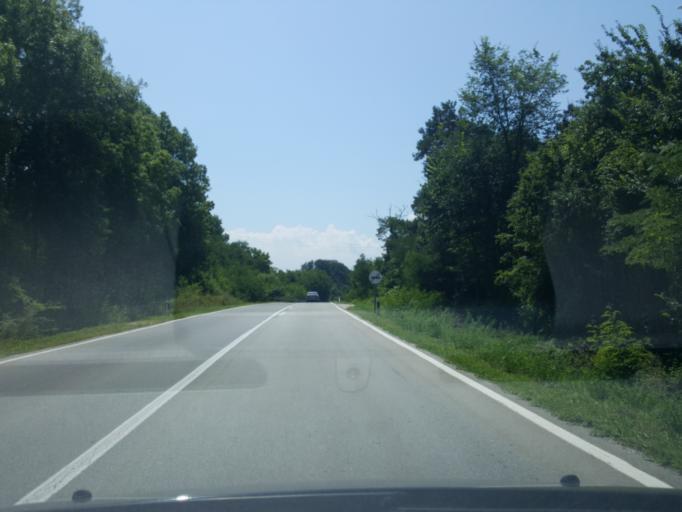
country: RS
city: Prislonica
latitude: 43.9576
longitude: 20.4164
